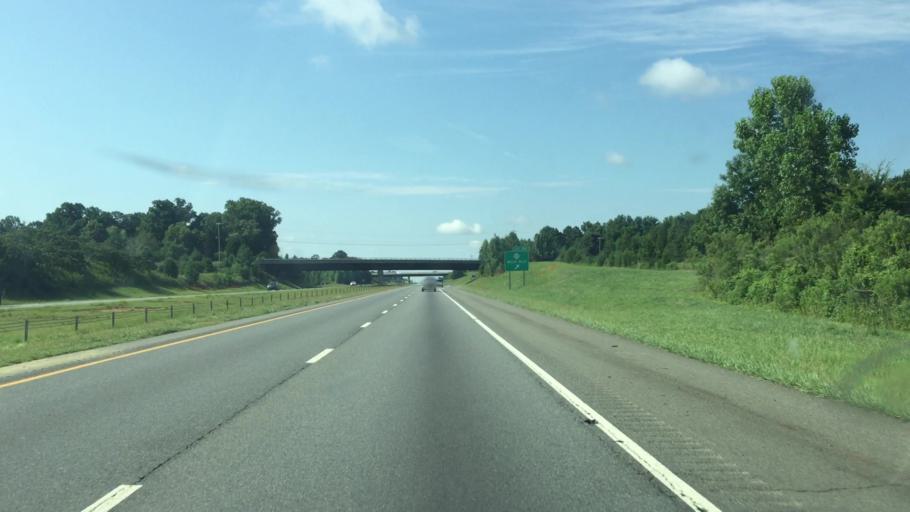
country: US
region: North Carolina
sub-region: Mecklenburg County
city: Mint Hill
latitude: 35.1854
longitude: -80.6296
